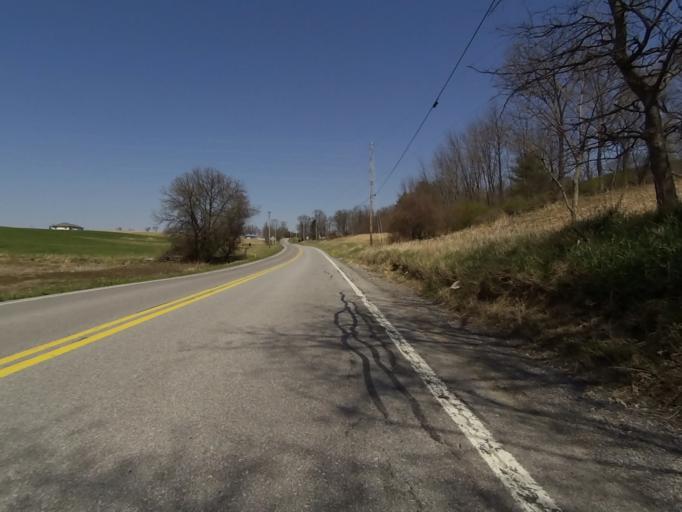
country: US
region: Pennsylvania
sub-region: Blair County
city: Tyrone
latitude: 40.5843
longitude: -78.1411
